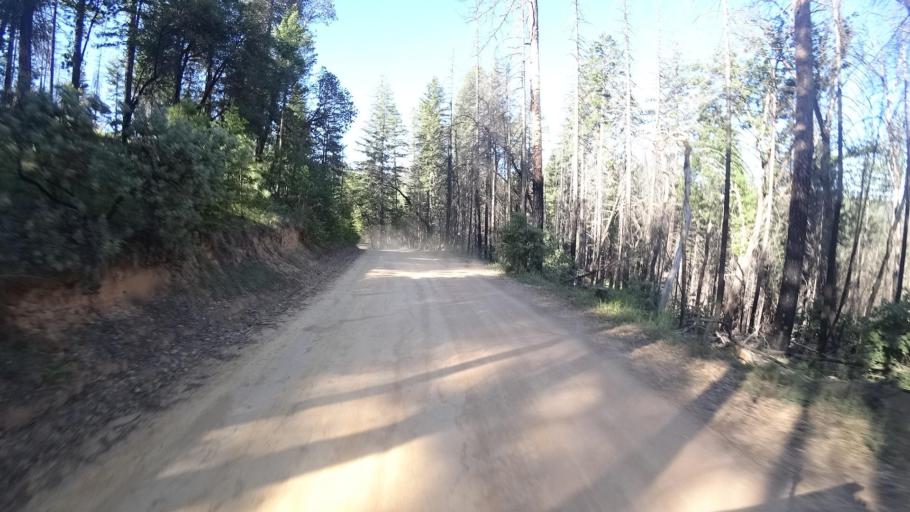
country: US
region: California
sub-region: Lake County
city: Upper Lake
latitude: 39.3834
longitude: -122.9840
